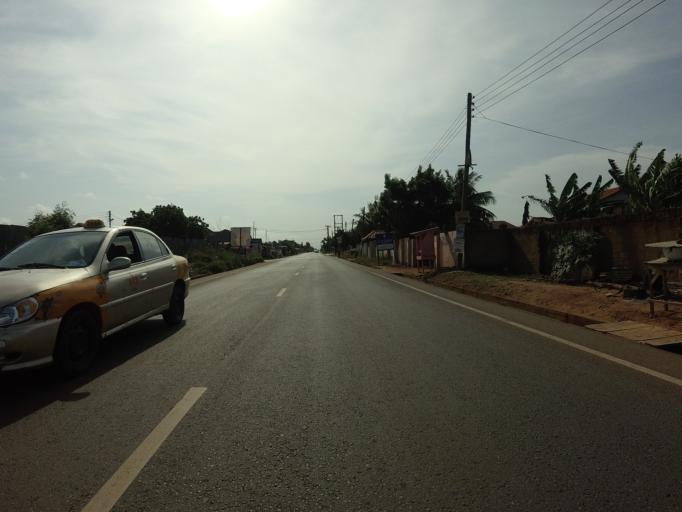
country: GH
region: Greater Accra
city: Nungua
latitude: 5.6451
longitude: -0.0813
